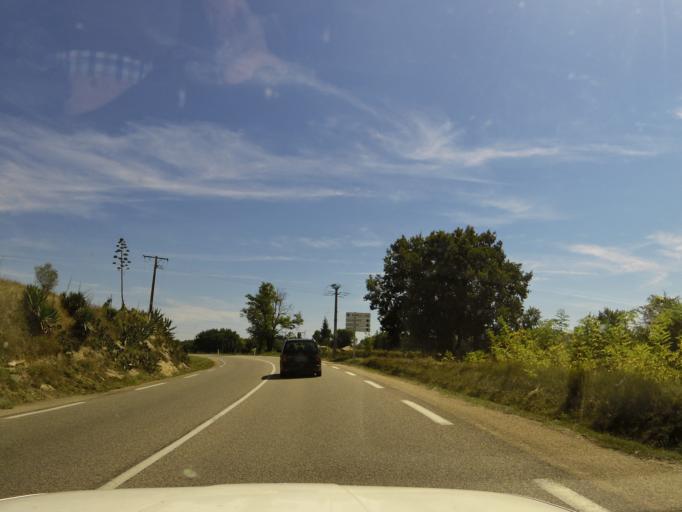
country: FR
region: Languedoc-Roussillon
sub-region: Departement du Gard
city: Bagnols-sur-Ceze
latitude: 44.1669
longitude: 4.5844
